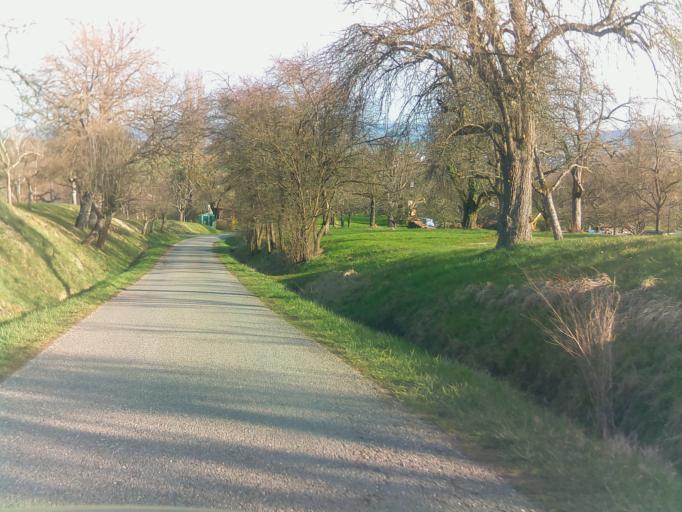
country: DE
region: Baden-Wuerttemberg
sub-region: Regierungsbezirk Stuttgart
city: Allmersbach im Tal
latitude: 48.9053
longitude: 9.4886
